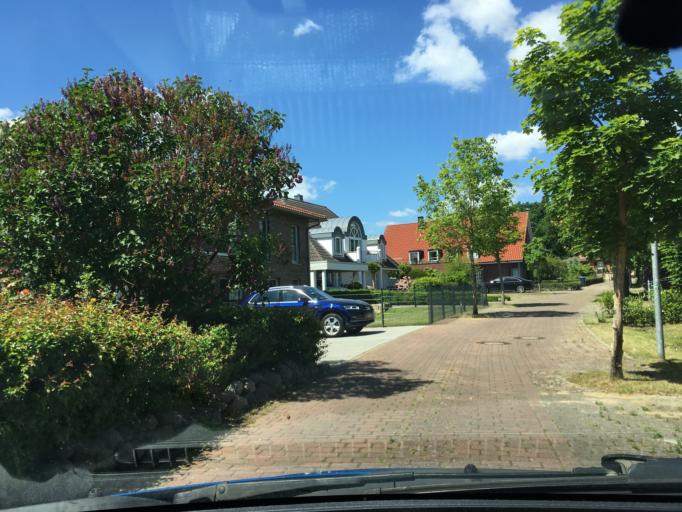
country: DE
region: Lower Saxony
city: Uelzen
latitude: 52.9647
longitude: 10.5284
